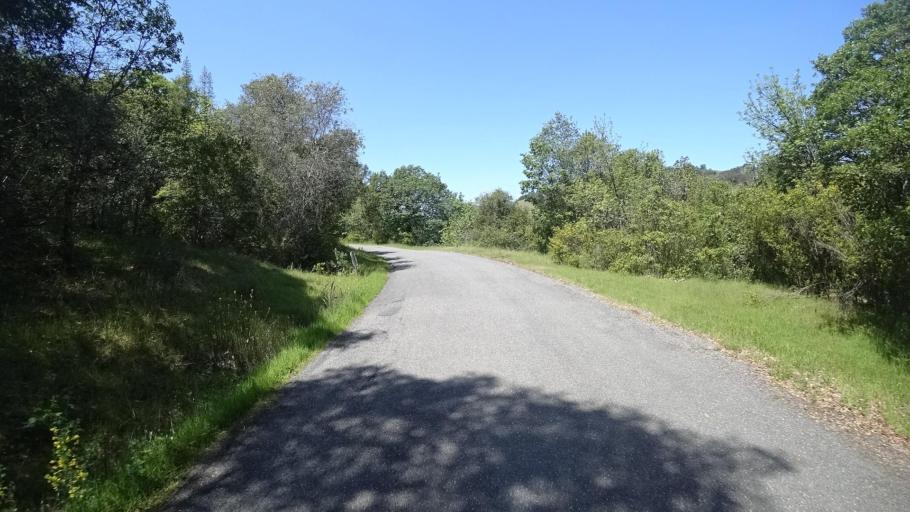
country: US
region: California
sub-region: Humboldt County
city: Redway
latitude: 40.1895
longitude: -123.5675
